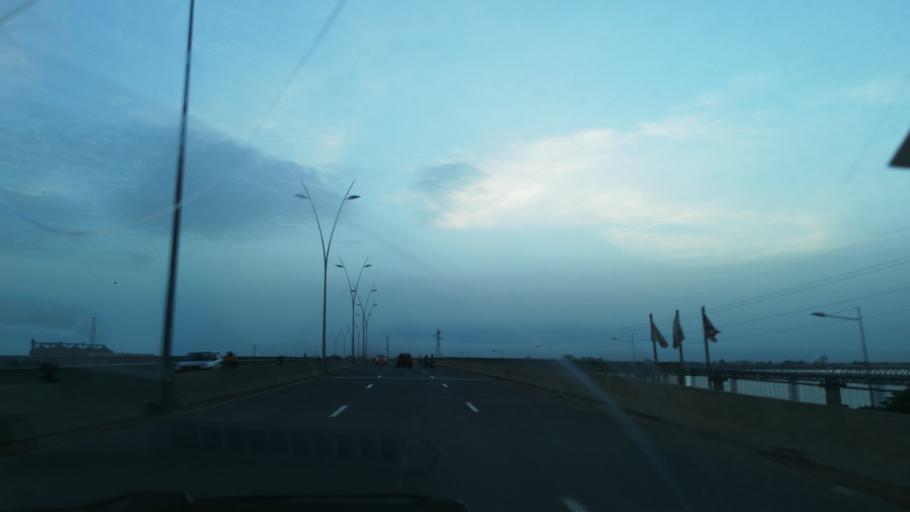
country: CM
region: Littoral
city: Bonaberi
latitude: 4.0724
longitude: 9.6967
